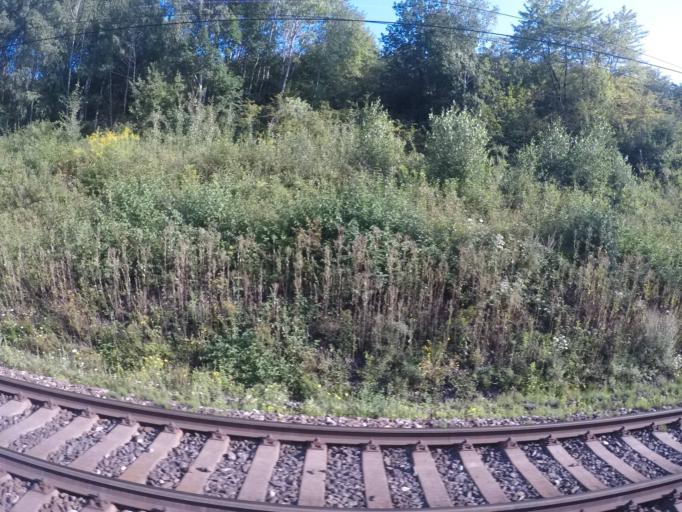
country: SK
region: Kosicky
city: Gelnica
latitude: 48.8736
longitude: 21.1041
